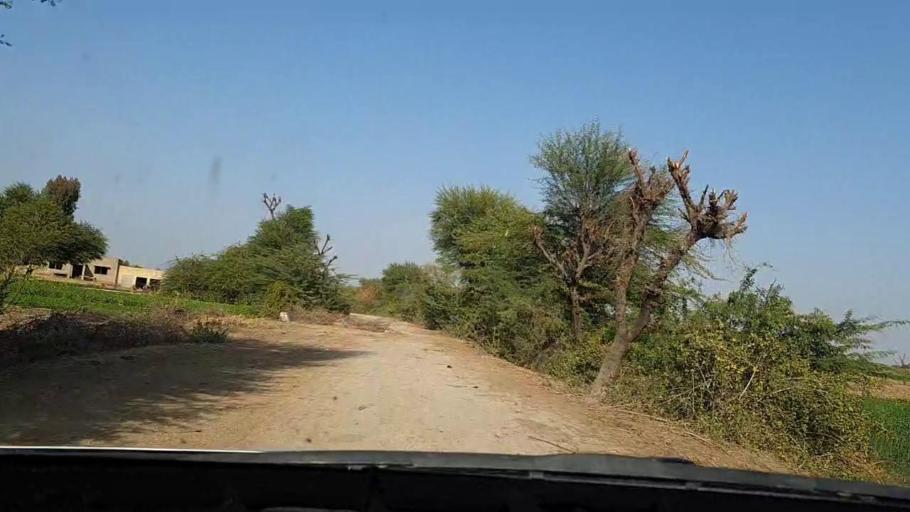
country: PK
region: Sindh
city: Tando Mittha Khan
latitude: 25.8099
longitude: 69.3279
